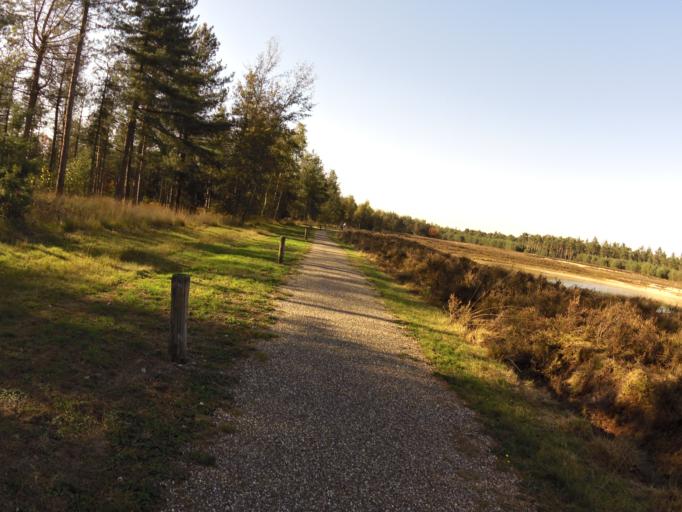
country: NL
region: North Brabant
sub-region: Gemeente Someren
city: Someren
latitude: 51.3706
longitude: 5.6547
